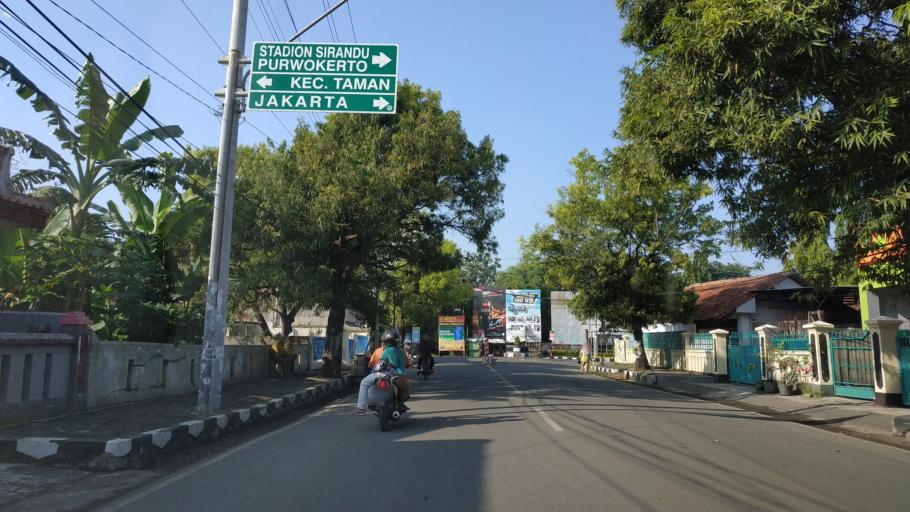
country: ID
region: Central Java
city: Pemalang
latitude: -6.9028
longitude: 109.3878
